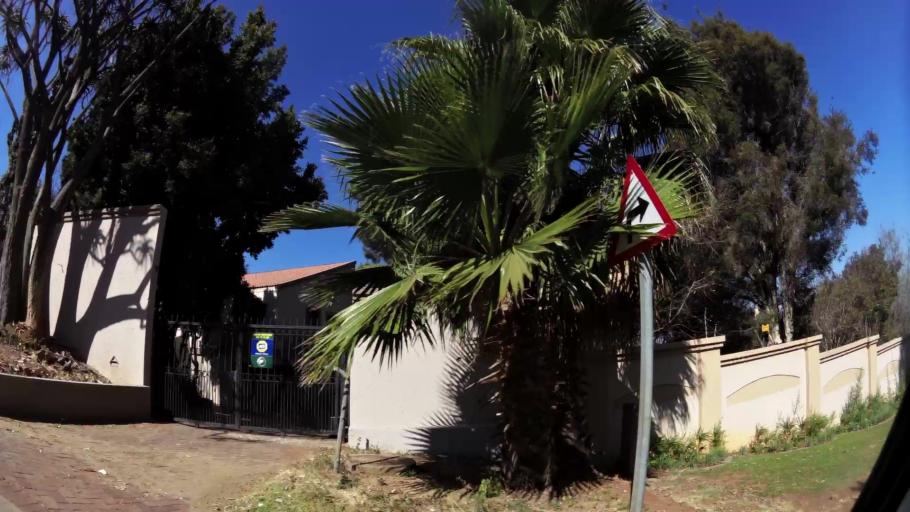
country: ZA
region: Gauteng
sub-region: City of Tshwane Metropolitan Municipality
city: Centurion
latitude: -25.8031
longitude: 28.2432
